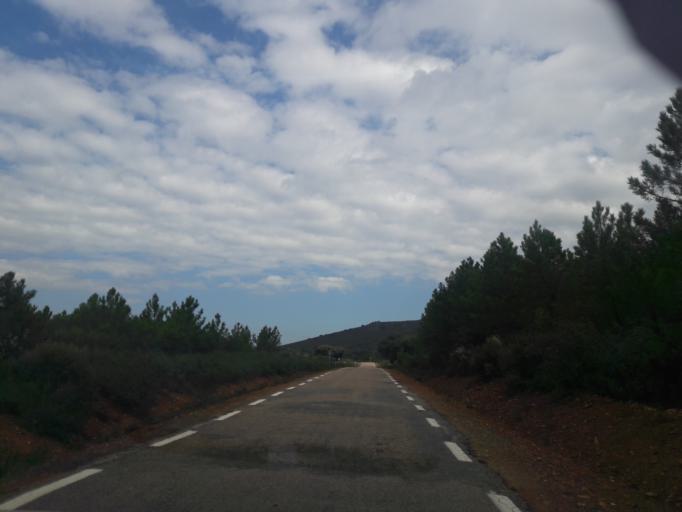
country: ES
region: Castille and Leon
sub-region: Provincia de Salamanca
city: Serradilla del Arroyo
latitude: 40.5348
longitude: -6.3828
